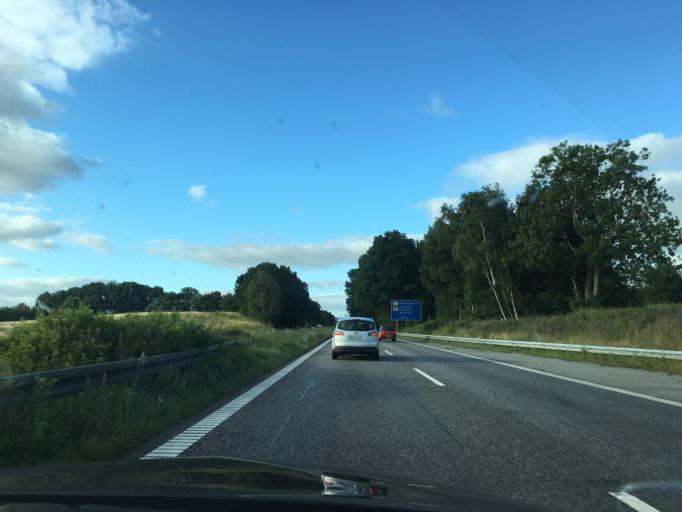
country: DK
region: Capital Region
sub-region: Horsholm Kommune
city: Horsholm
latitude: 55.8890
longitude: 12.4771
